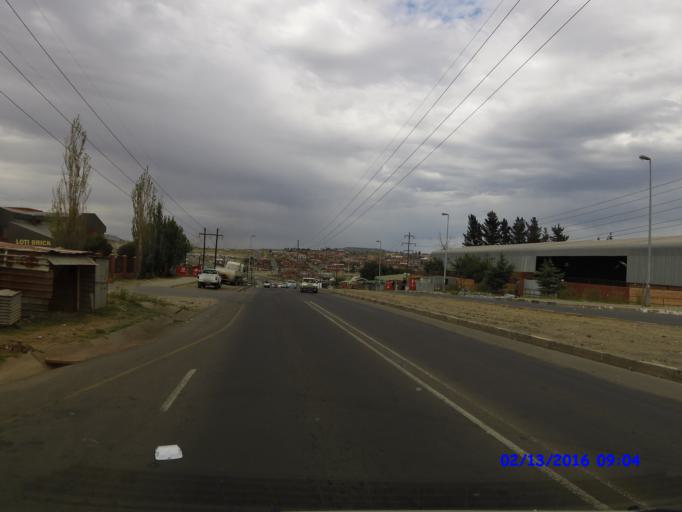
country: LS
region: Maseru
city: Maseru
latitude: -29.3409
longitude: 27.4612
